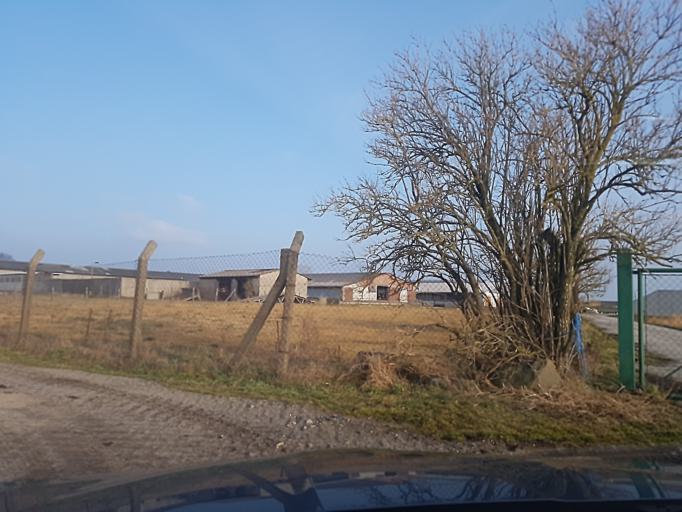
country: DE
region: Brandenburg
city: Ruckersdorf
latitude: 51.5885
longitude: 13.5358
